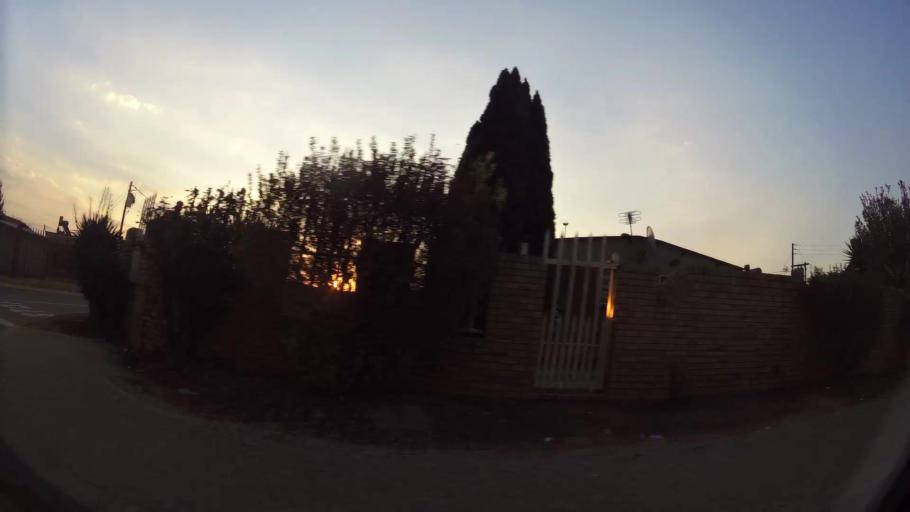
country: ZA
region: Gauteng
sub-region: Ekurhuleni Metropolitan Municipality
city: Springs
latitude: -26.2659
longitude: 28.3947
